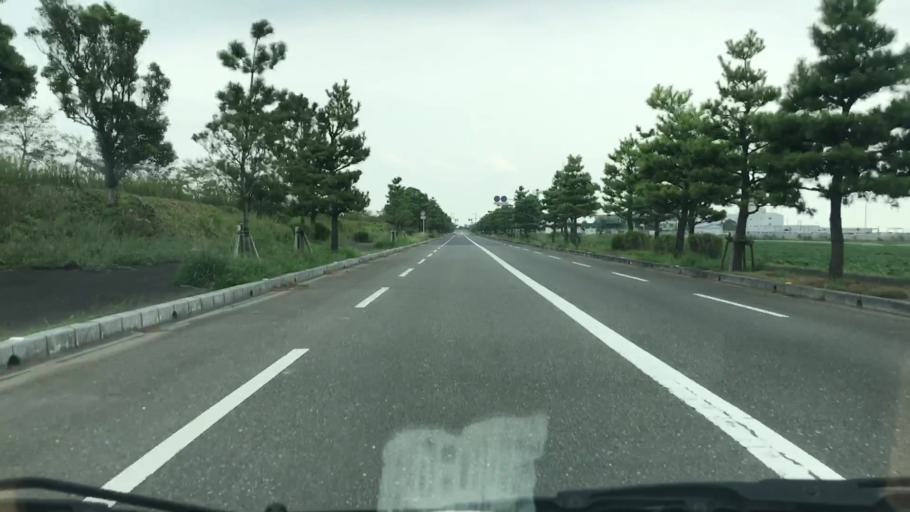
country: JP
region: Saga Prefecture
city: Okawa
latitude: 33.1569
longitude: 130.2978
